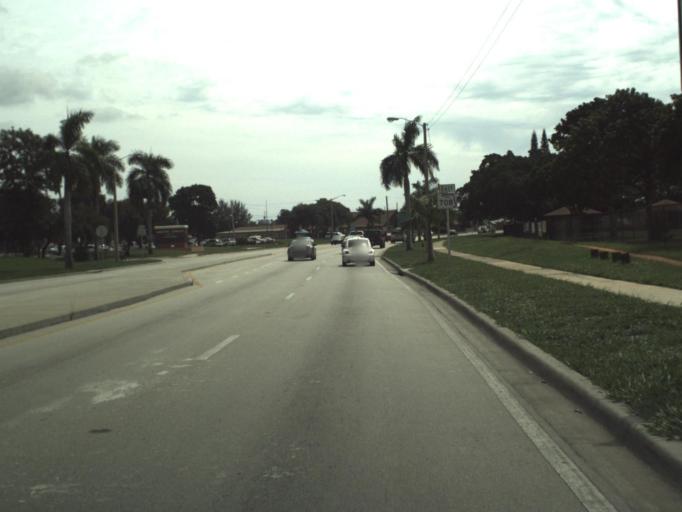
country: US
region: Florida
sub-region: Palm Beach County
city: Riviera Beach
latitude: 26.7825
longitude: -80.0661
